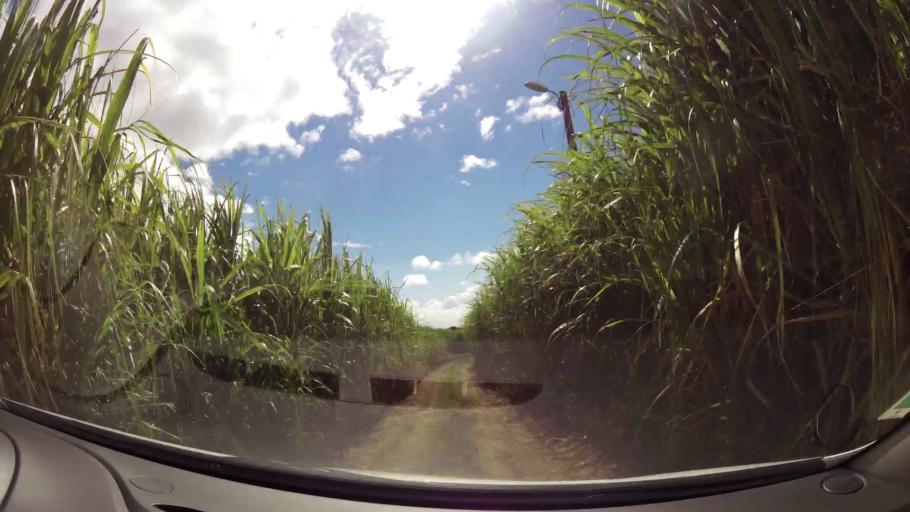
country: RE
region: Reunion
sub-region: Reunion
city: Sainte-Marie
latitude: -20.9298
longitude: 55.5024
